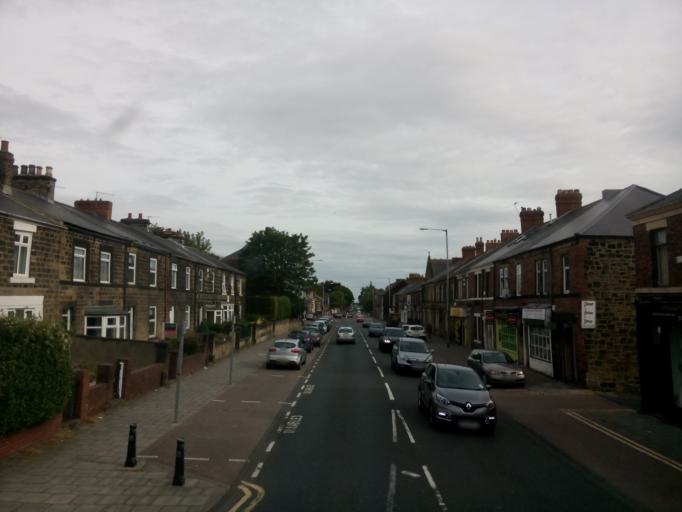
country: GB
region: England
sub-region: Gateshead
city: Lamesley
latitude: 54.9327
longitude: -1.5986
